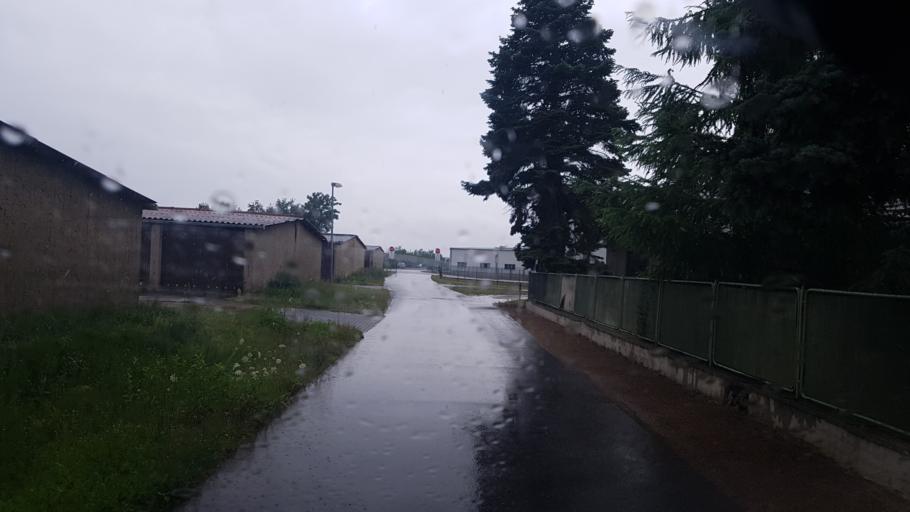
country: DE
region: Brandenburg
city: Dahme
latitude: 51.8668
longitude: 13.4129
